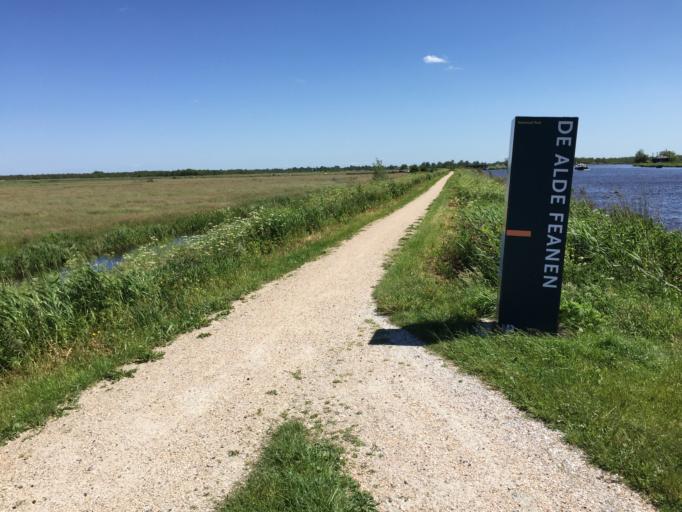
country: NL
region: Friesland
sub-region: Gemeente Boarnsterhim
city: Warten
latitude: 53.1426
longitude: 5.9116
